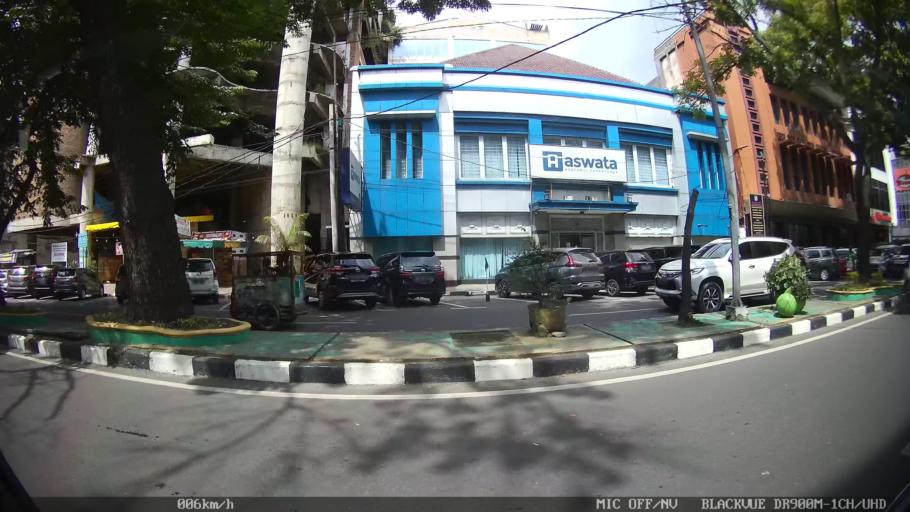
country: ID
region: North Sumatra
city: Medan
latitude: 3.5820
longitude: 98.6822
